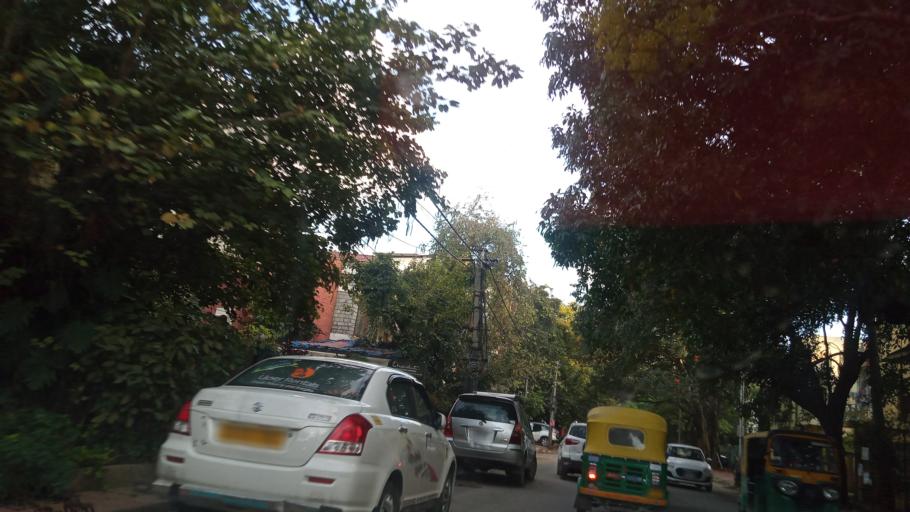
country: IN
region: Karnataka
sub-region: Bangalore Urban
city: Bangalore
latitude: 12.9325
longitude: 77.6279
